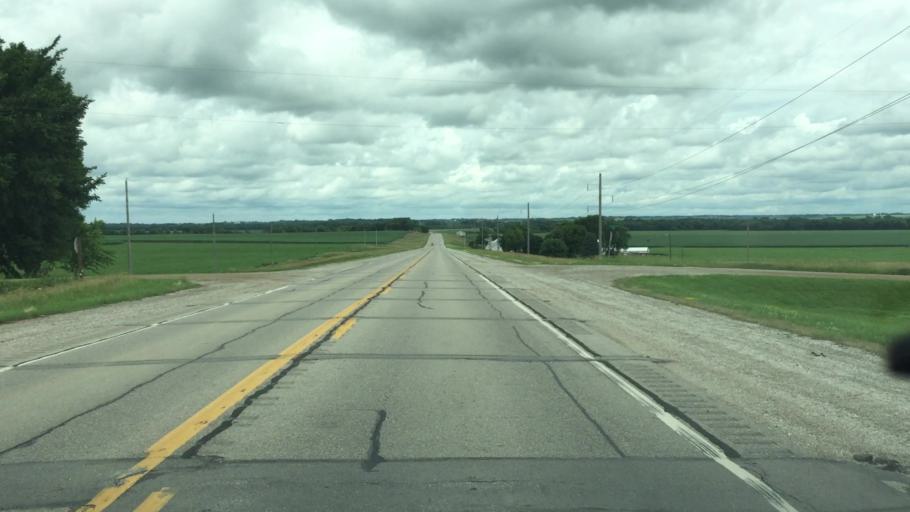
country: US
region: Iowa
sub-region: Jasper County
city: Monroe
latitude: 41.5948
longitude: -93.0967
